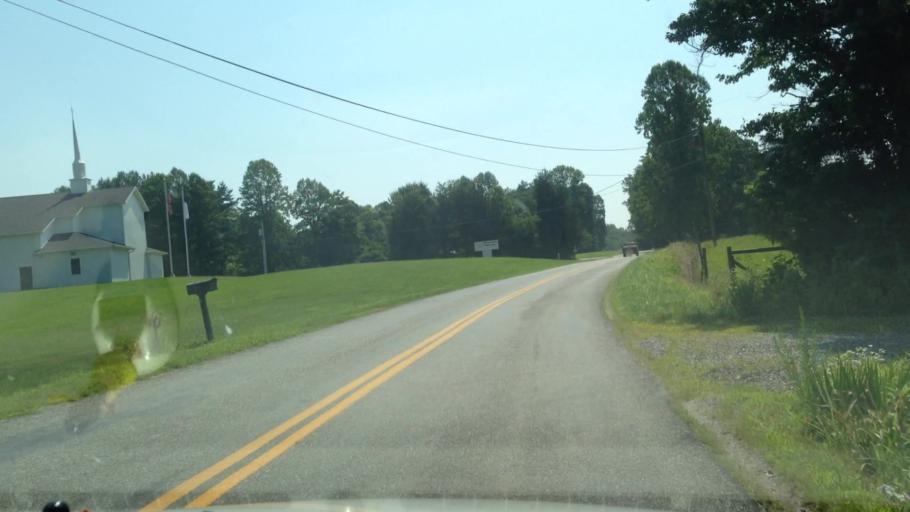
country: US
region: Virginia
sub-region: Patrick County
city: Stuart
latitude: 36.5785
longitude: -80.2482
